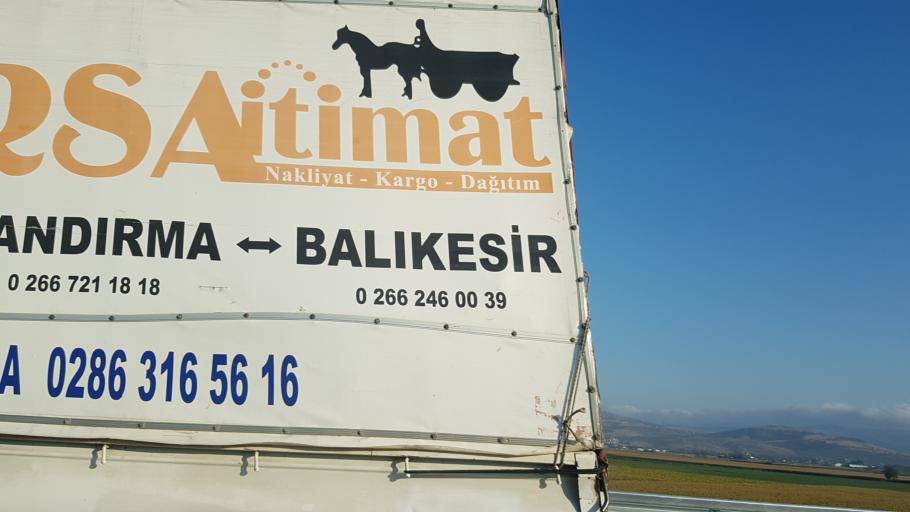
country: TR
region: Bursa
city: Karacabey
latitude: 40.2146
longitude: 28.3921
